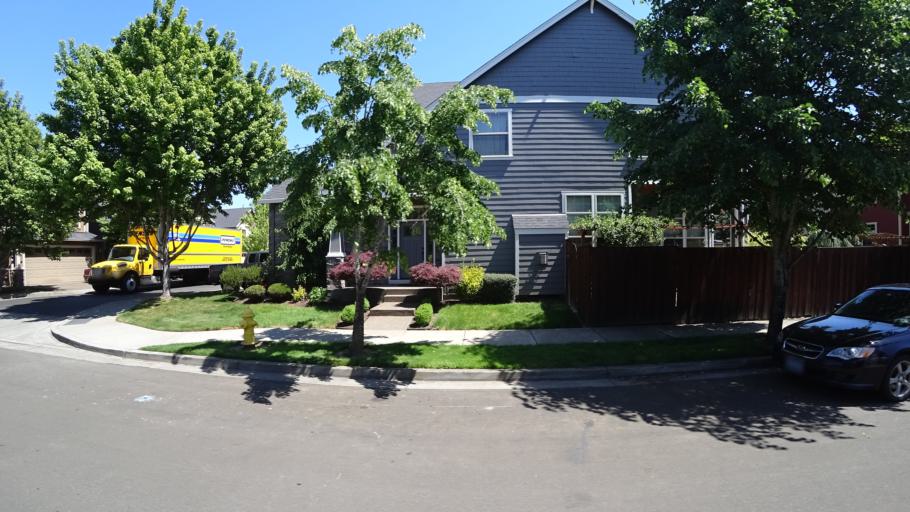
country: US
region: Oregon
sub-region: Washington County
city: Rockcreek
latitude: 45.5259
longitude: -122.9134
